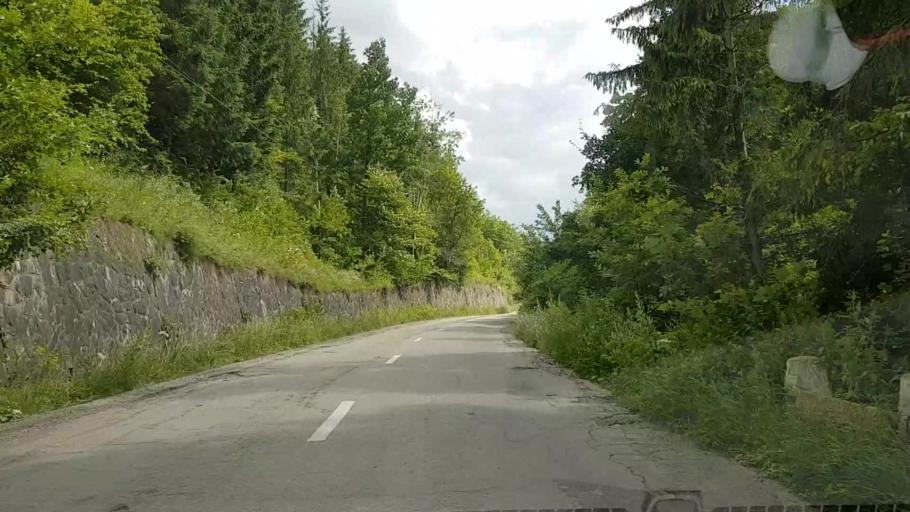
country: RO
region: Neamt
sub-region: Comuna Hangu
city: Hangu
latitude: 47.0546
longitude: 26.0380
